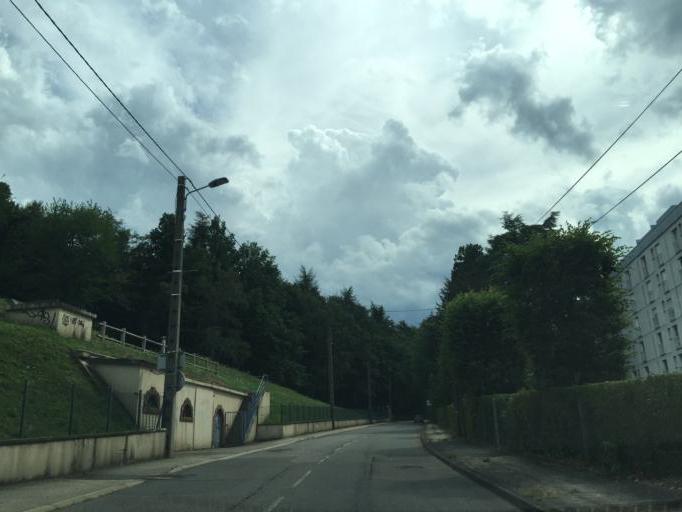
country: FR
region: Rhone-Alpes
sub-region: Departement de la Loire
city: Saint-Etienne
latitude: 45.4156
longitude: 4.4107
